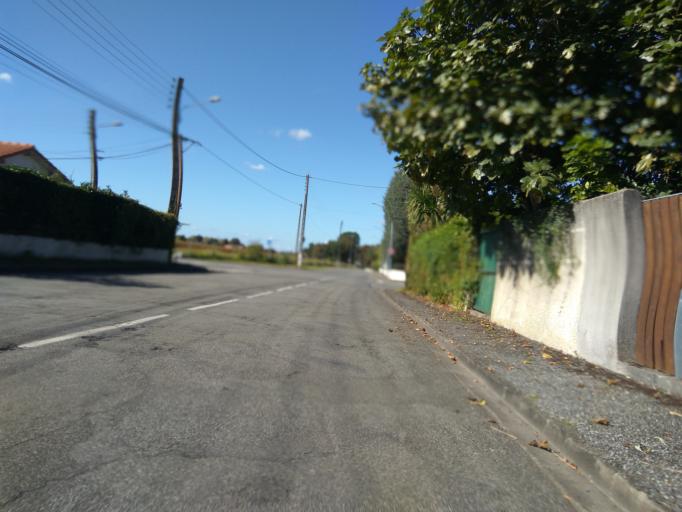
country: FR
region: Aquitaine
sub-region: Departement des Pyrenees-Atlantiques
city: Idron
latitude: 43.3008
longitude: -0.3199
